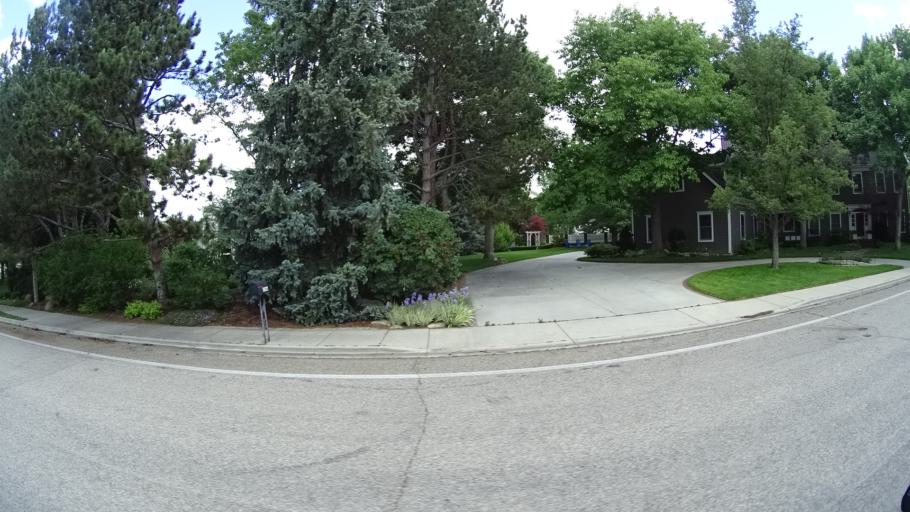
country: US
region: Idaho
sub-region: Ada County
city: Boise
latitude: 43.5838
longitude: -116.1665
